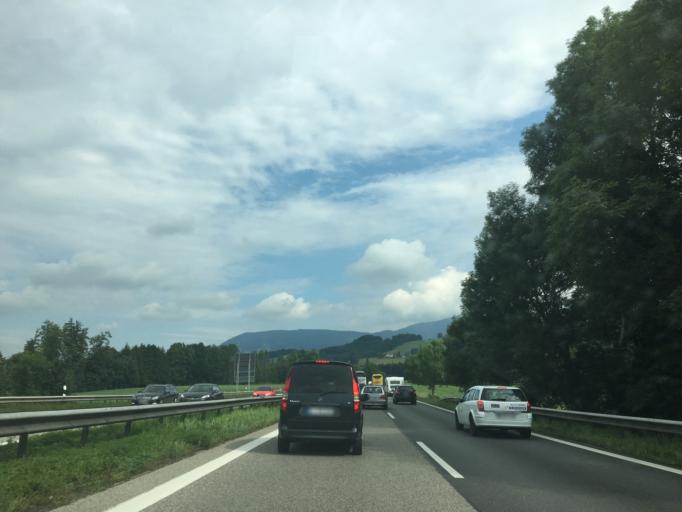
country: DE
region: Bavaria
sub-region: Upper Bavaria
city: Rohrdorf
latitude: 47.8002
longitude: 12.1916
